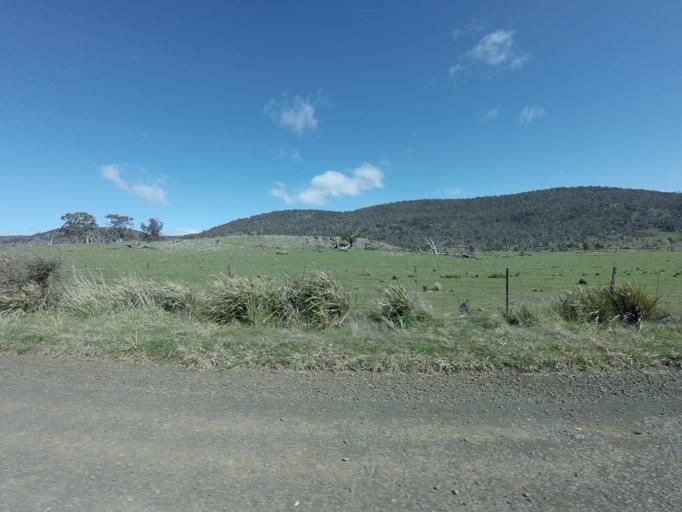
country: AU
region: Tasmania
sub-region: Northern Midlands
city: Evandale
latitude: -41.9392
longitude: 147.4230
